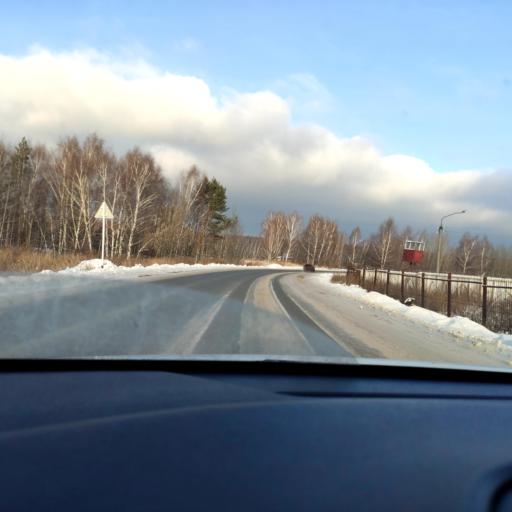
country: RU
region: Tatarstan
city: Osinovo
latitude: 55.8951
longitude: 48.8899
